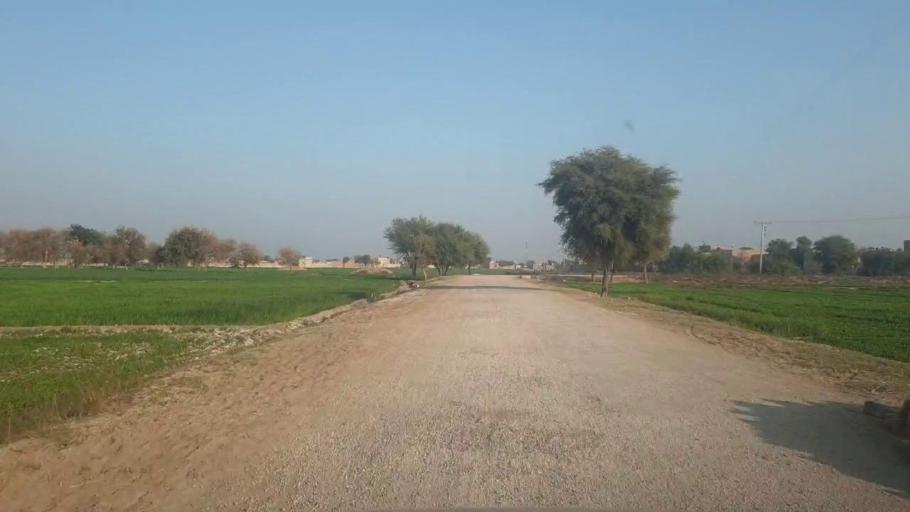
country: PK
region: Sindh
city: Sakrand
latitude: 26.0550
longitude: 68.3922
